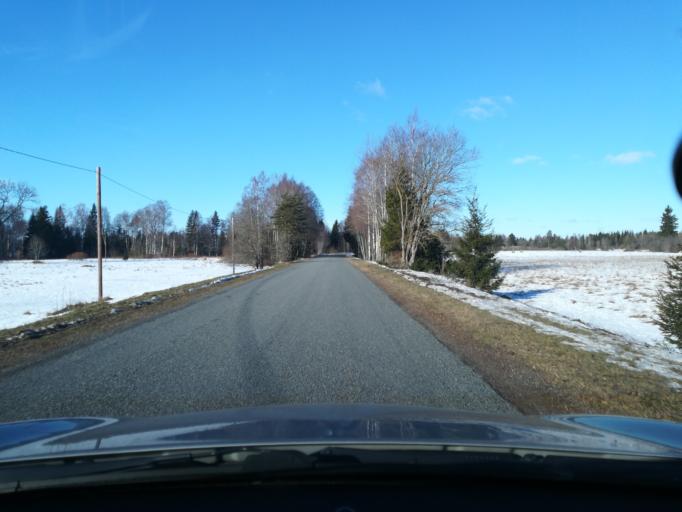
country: EE
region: Raplamaa
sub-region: Kohila vald
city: Kohila
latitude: 59.2372
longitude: 24.7557
